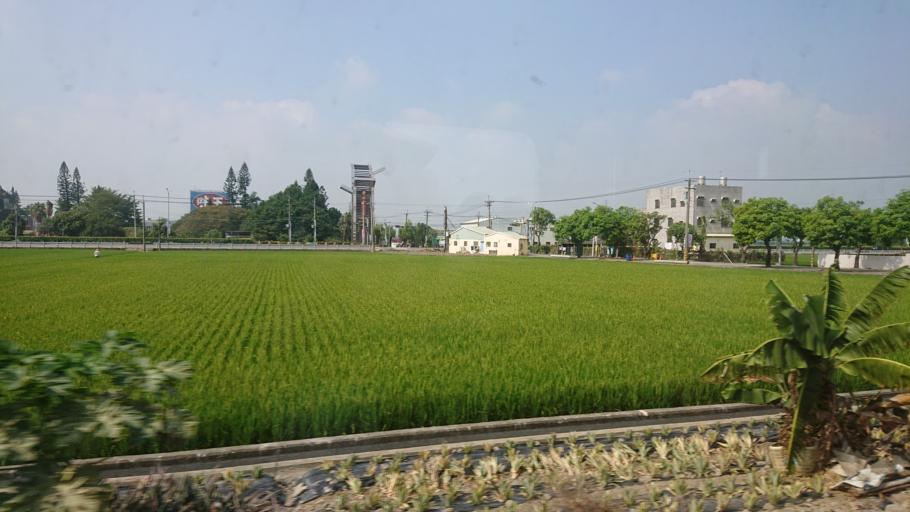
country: TW
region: Taiwan
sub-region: Yunlin
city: Douliu
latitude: 23.6425
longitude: 120.4714
